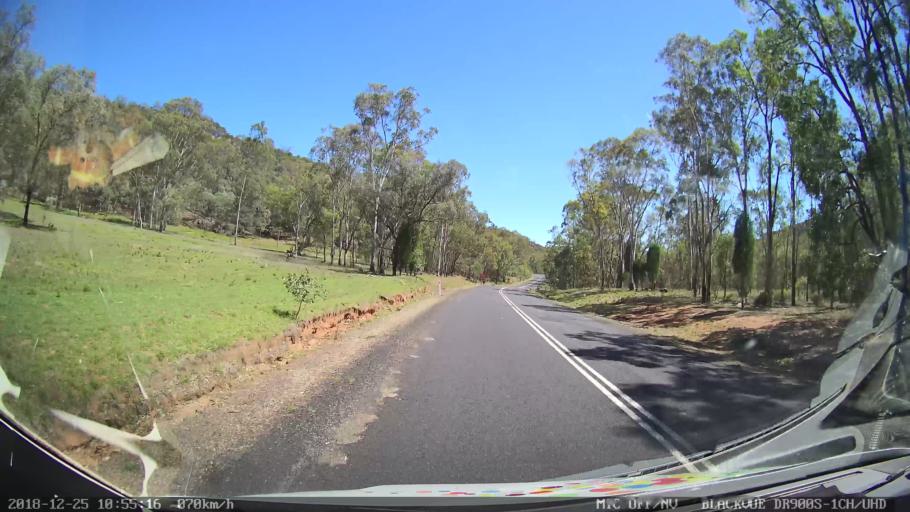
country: AU
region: New South Wales
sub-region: Upper Hunter Shire
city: Merriwa
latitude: -32.4008
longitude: 150.2723
